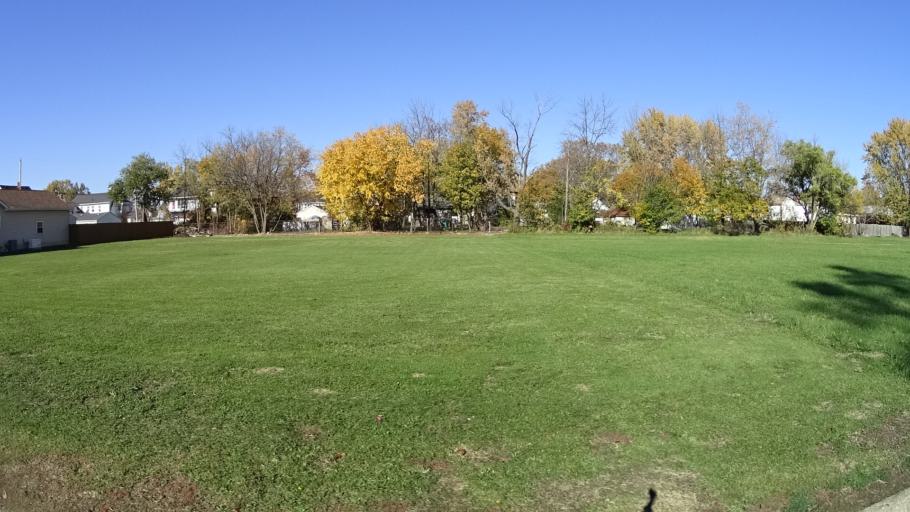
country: US
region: Ohio
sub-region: Lorain County
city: Lorain
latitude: 41.4595
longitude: -82.1885
